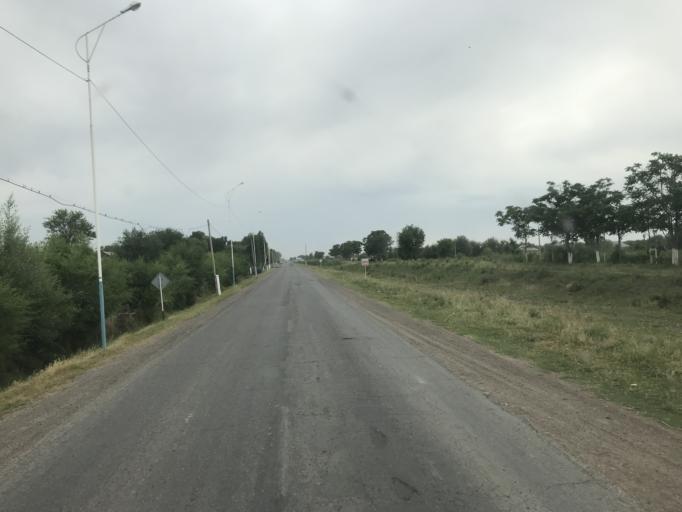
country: KZ
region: Ongtustik Qazaqstan
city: Asykata
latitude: 40.9393
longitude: 68.4132
